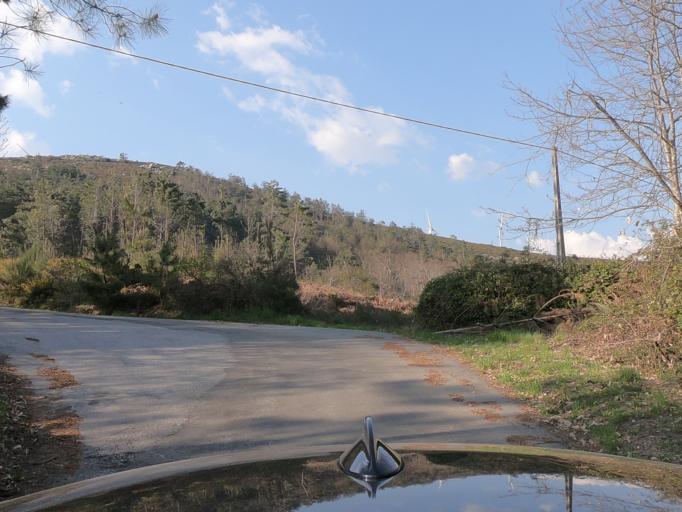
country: PT
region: Vila Real
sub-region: Vila Real
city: Vila Real
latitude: 41.3164
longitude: -7.8631
